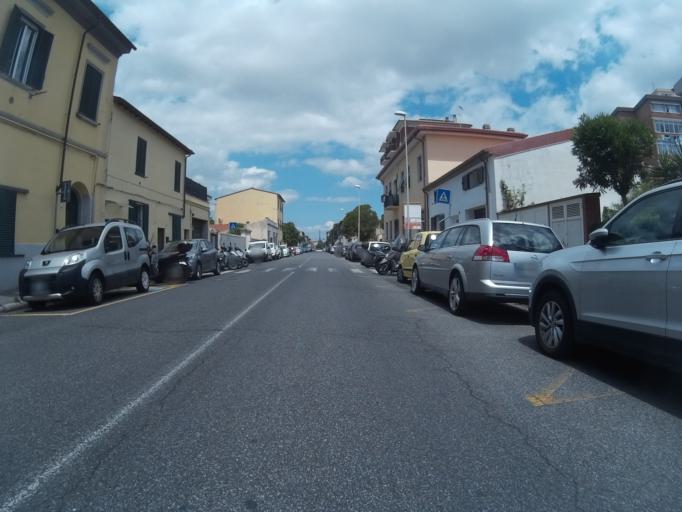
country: IT
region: Tuscany
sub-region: Provincia di Livorno
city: Livorno
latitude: 43.5642
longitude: 10.3307
